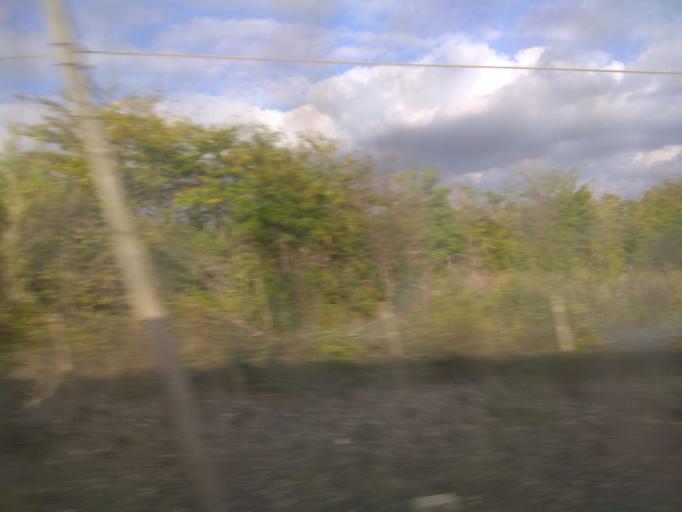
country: IT
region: Latium
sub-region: Citta metropolitana di Roma Capitale
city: Maccarese
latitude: 41.9080
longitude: 12.2084
